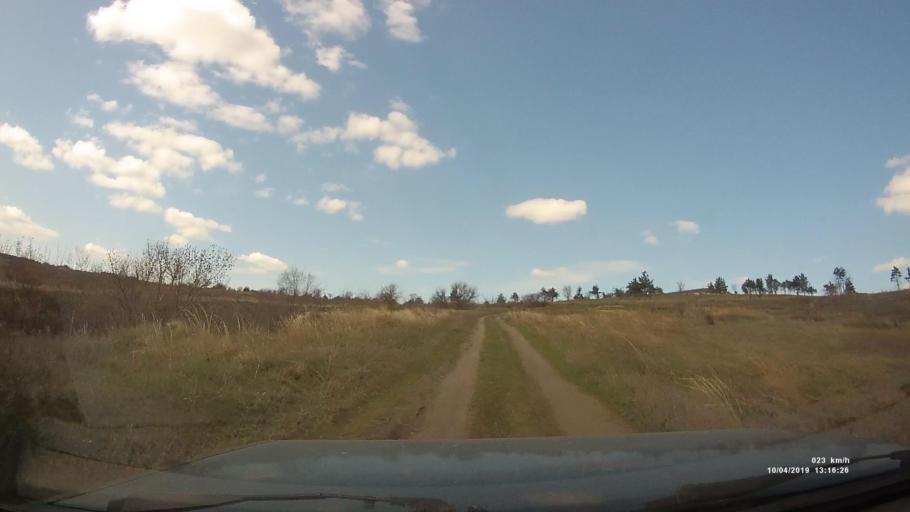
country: RU
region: Rostov
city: Masalovka
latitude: 48.4209
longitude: 40.2560
